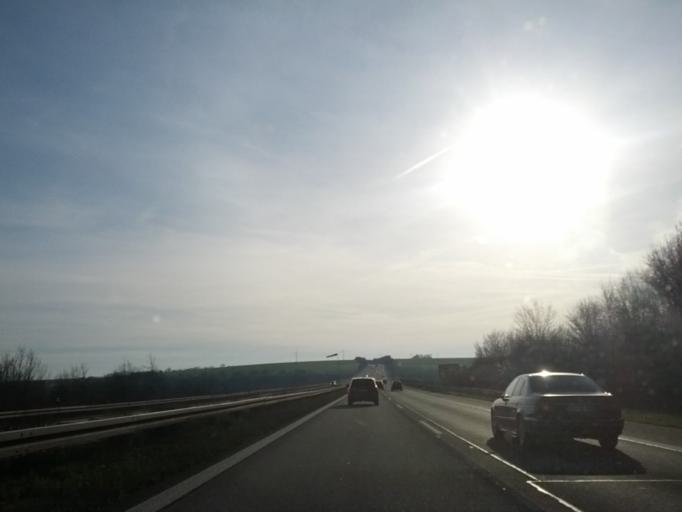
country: DE
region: Bavaria
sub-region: Regierungsbezirk Unterfranken
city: Segnitz
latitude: 49.6739
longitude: 10.1262
